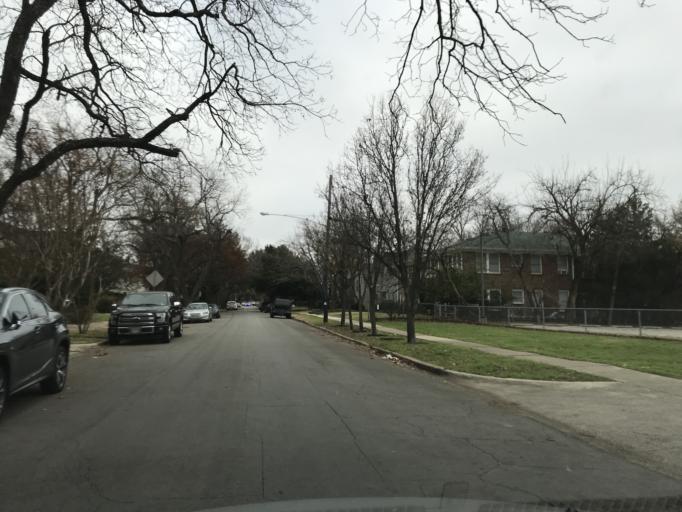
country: US
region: Texas
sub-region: Dallas County
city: Highland Park
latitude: 32.8217
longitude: -96.8096
